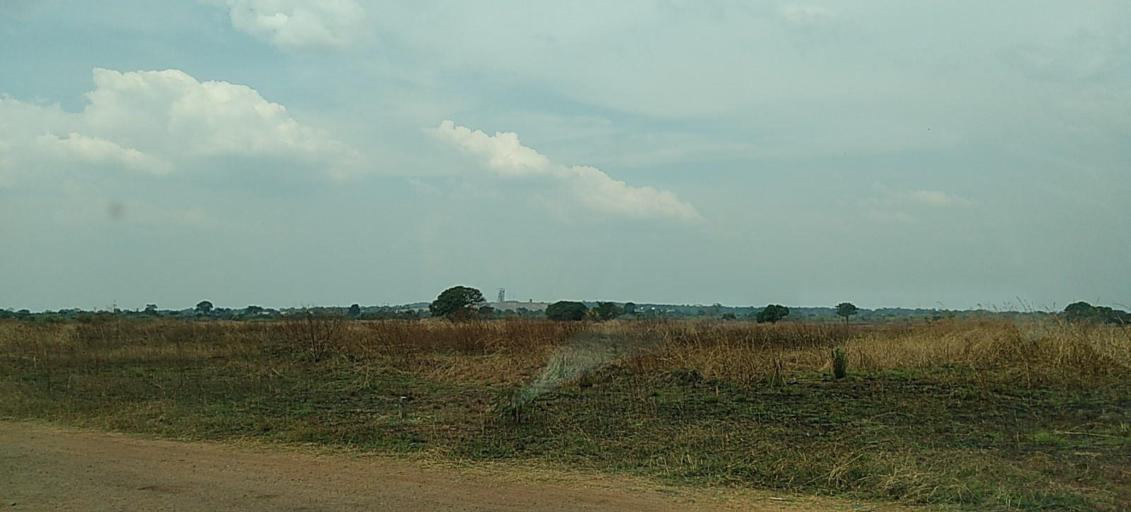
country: ZM
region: Copperbelt
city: Chililabombwe
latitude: -12.3936
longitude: 27.8061
